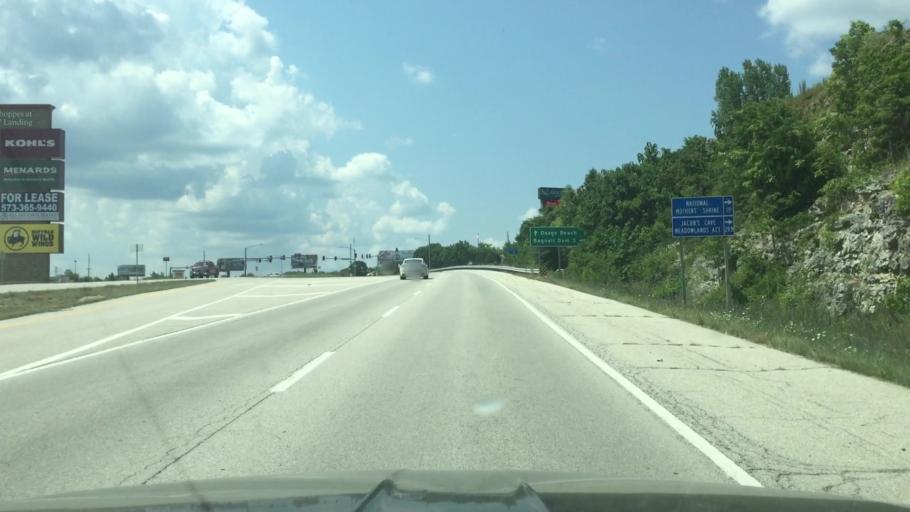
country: US
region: Missouri
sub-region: Miller County
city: Lake Ozark
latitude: 38.1777
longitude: -92.6142
